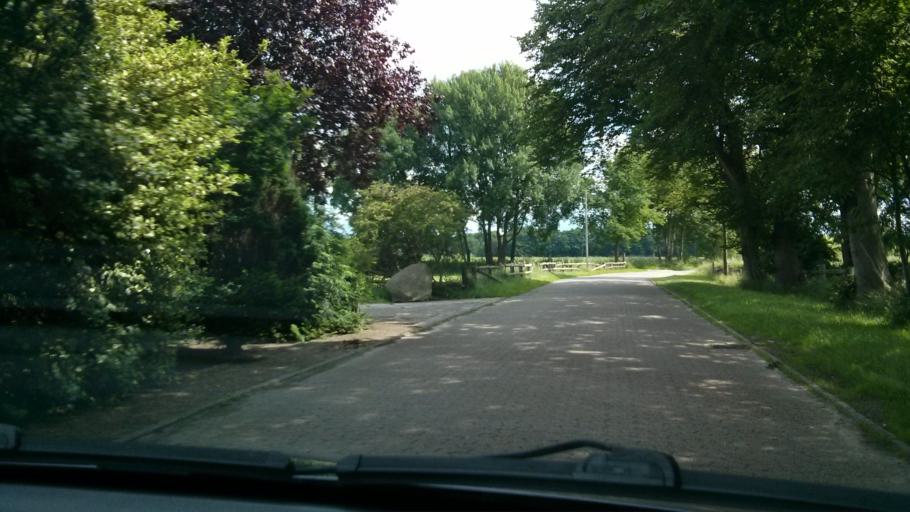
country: DE
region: Lower Saxony
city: Schiffdorf
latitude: 53.5082
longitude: 8.6960
